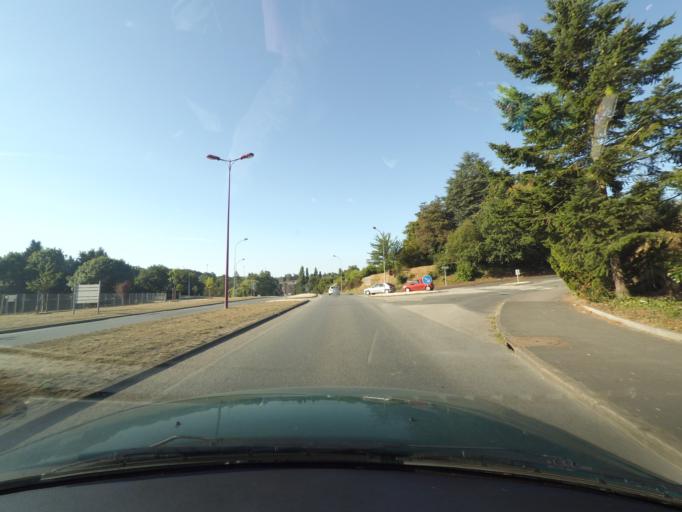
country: FR
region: Poitou-Charentes
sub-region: Departement des Deux-Sevres
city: Chatillon-sur-Thouet
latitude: 46.6596
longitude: -0.2396
